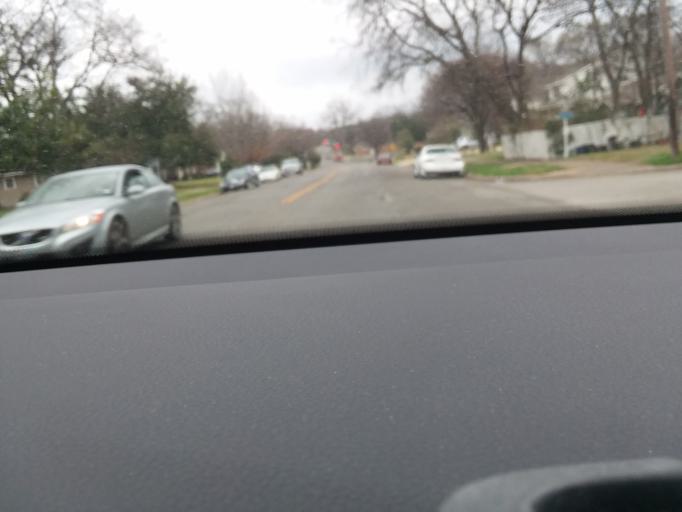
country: US
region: Texas
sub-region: Dallas County
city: Highland Park
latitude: 32.8160
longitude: -96.7638
